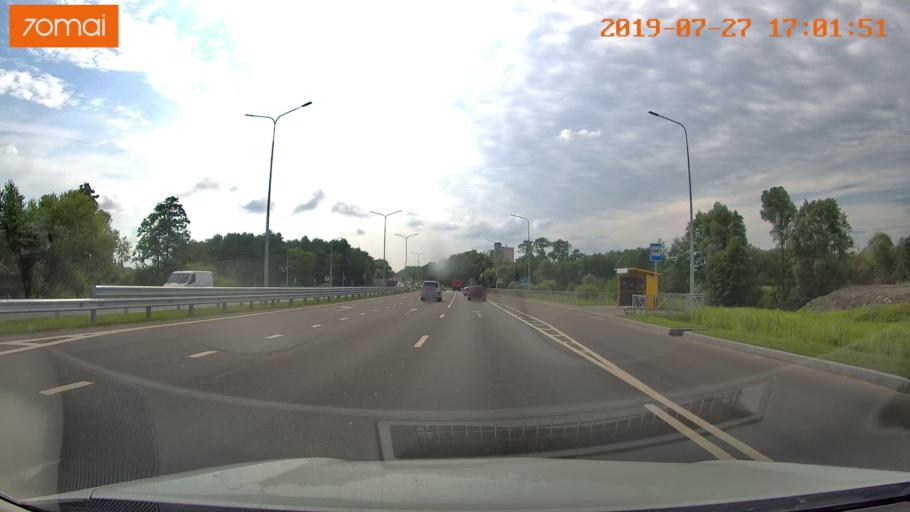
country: RU
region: Kaliningrad
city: Bol'shoe Isakovo
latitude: 54.7074
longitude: 20.6243
